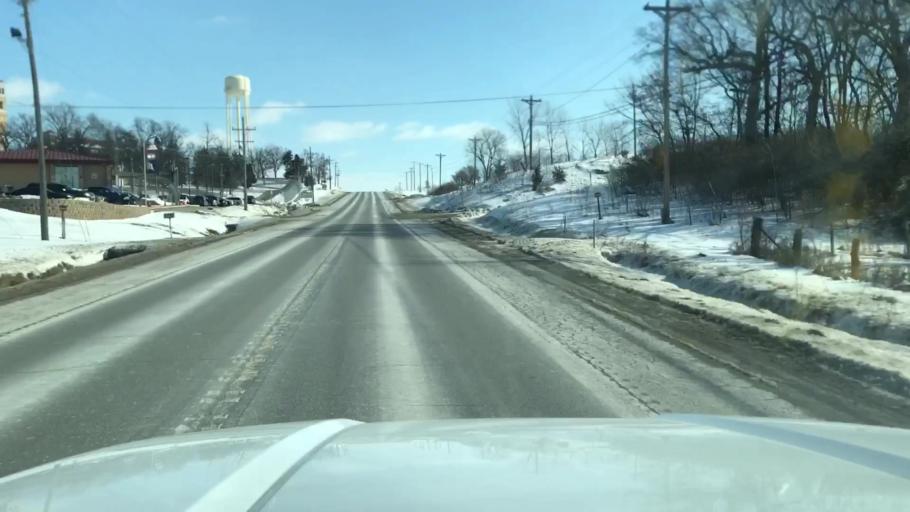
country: US
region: Missouri
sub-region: Nodaway County
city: Maryville
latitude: 40.3448
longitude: -94.8170
